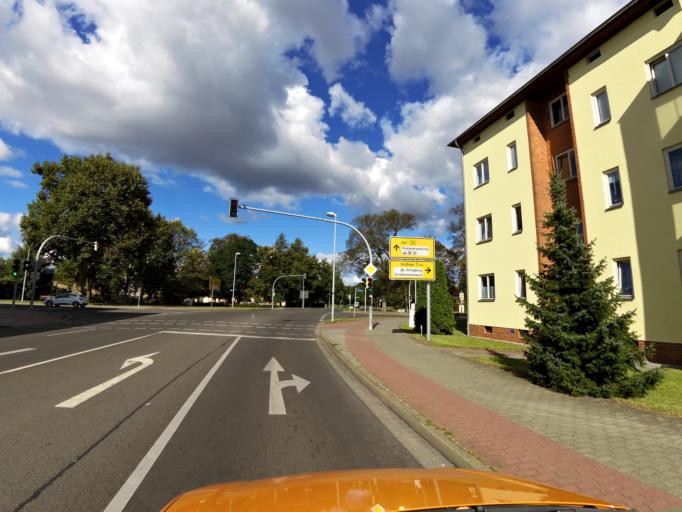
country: DE
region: Brandenburg
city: Luckenwalde
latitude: 52.0846
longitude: 13.1803
